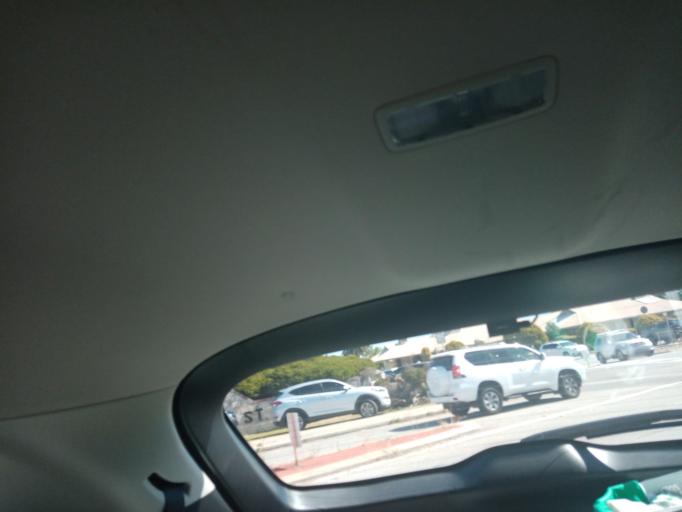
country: AU
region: Western Australia
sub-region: City of Cockburn
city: Spearwood
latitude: -32.1203
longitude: 115.7826
